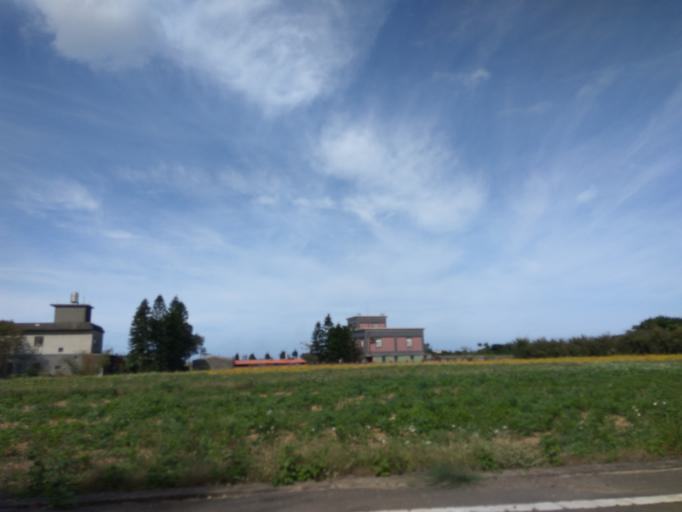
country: TW
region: Taiwan
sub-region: Hsinchu
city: Zhubei
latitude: 25.0170
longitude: 121.0814
